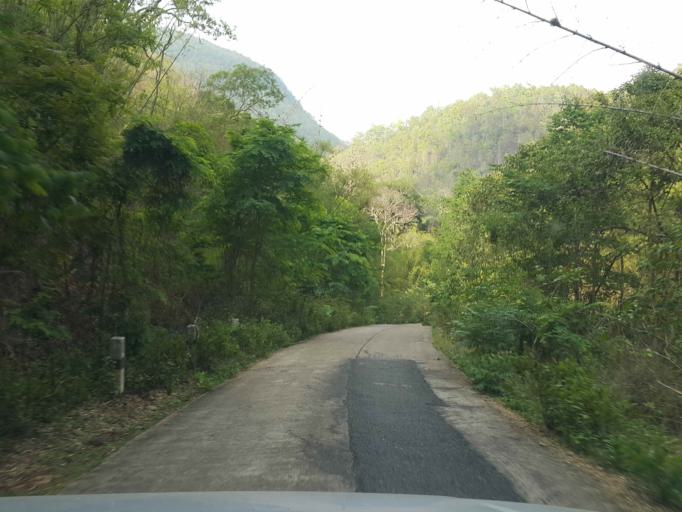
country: TH
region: Chiang Mai
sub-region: Amphoe Chiang Dao
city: Chiang Dao
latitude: 19.3940
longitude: 98.7714
